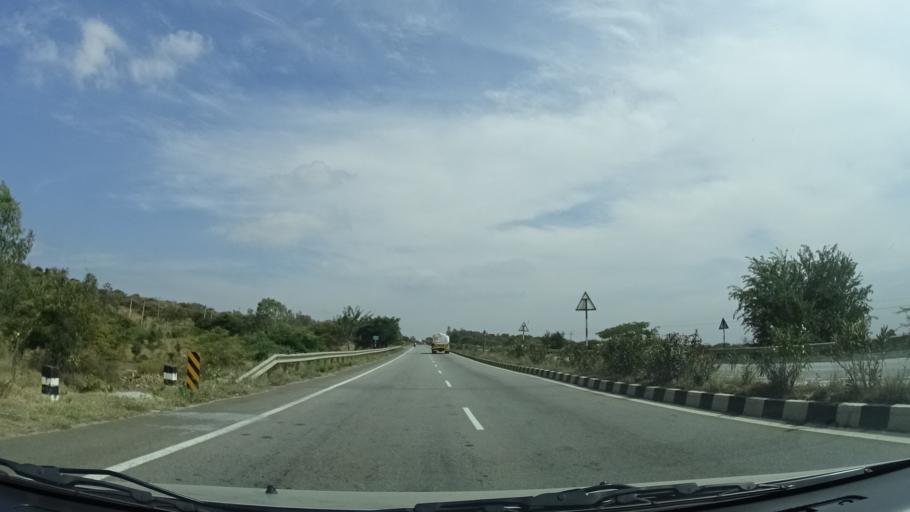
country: IN
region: Karnataka
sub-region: Chikkaballapur
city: Chik Ballapur
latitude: 13.5485
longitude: 77.7744
